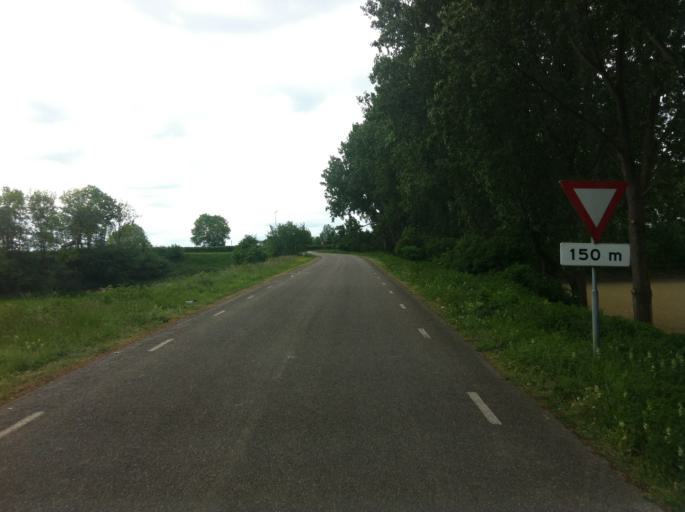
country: NL
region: Limburg
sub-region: Gemeente Roermond
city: Roermond
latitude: 51.2037
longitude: 5.9594
